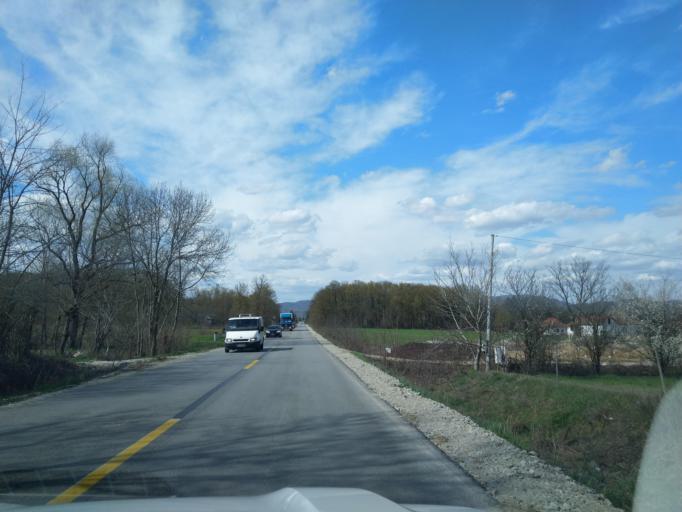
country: RS
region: Central Serbia
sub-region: Zlatiborski Okrug
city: Arilje
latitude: 43.8038
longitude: 20.0942
